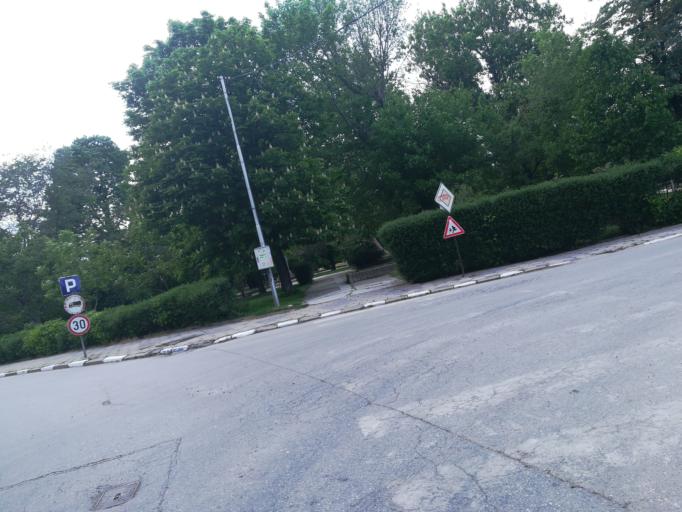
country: BG
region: Stara Zagora
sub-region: Obshtina Chirpan
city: Chirpan
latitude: 42.0982
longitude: 25.2280
